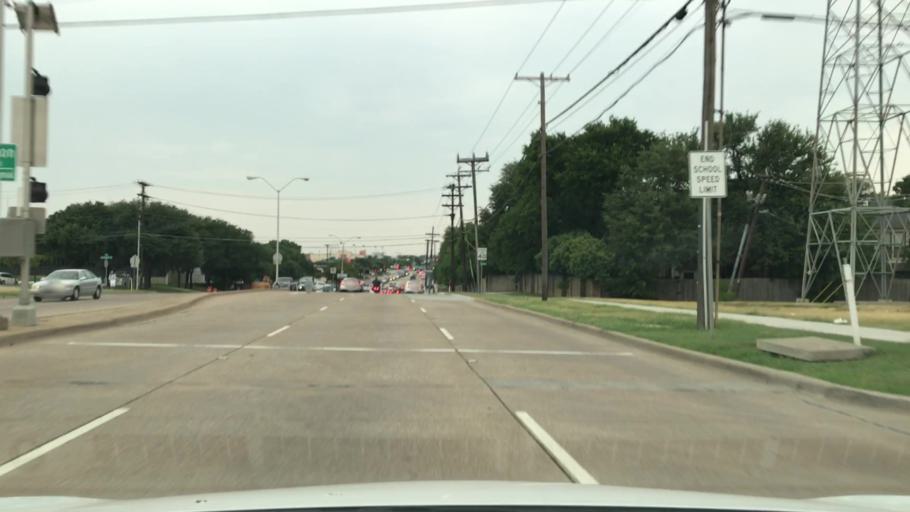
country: US
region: Texas
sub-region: Dallas County
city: Carrollton
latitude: 32.9778
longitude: -96.8902
